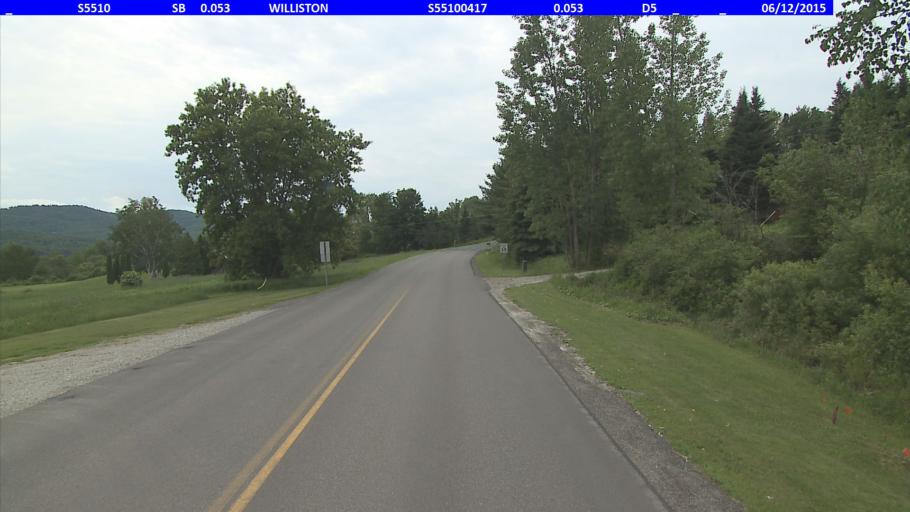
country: US
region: Vermont
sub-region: Chittenden County
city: Hinesburg
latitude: 44.3737
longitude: -73.0932
